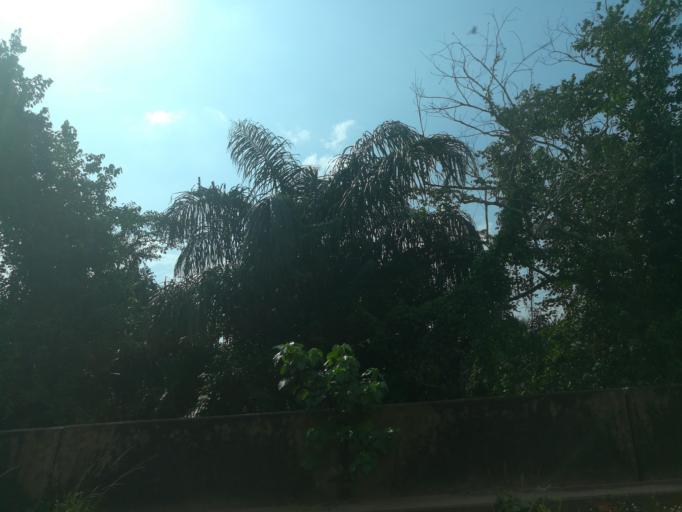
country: NG
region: Lagos
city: Ikorodu
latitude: 6.6268
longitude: 3.6644
